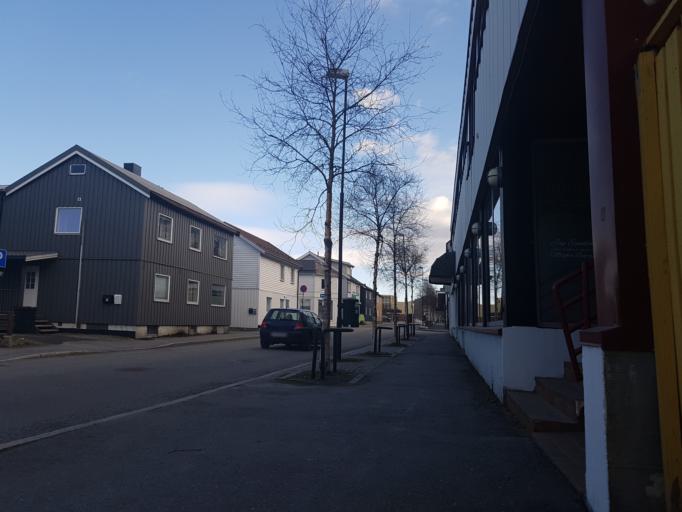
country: NO
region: Nordland
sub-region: Vefsn
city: Mosjoen
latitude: 65.8392
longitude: 13.1908
